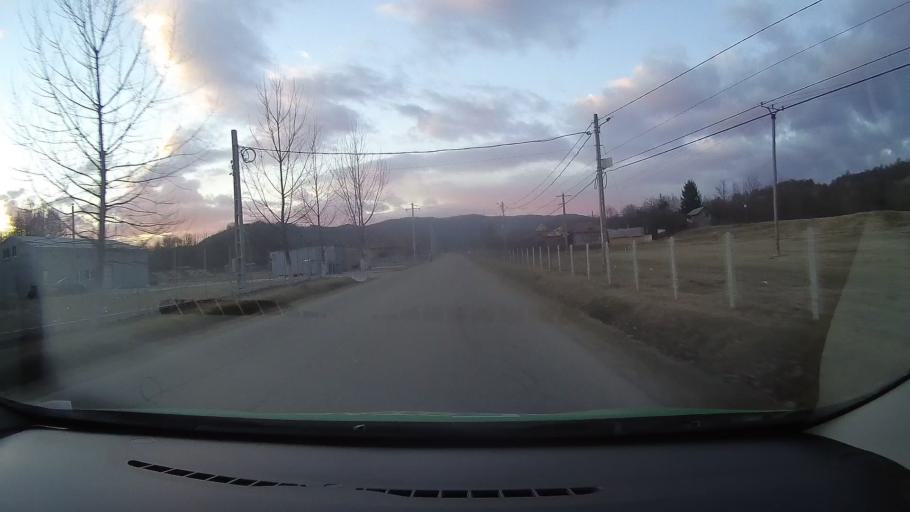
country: RO
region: Dambovita
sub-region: Comuna Valea Lunga
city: Valea Lunga-Cricov
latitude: 45.0631
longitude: 25.5884
